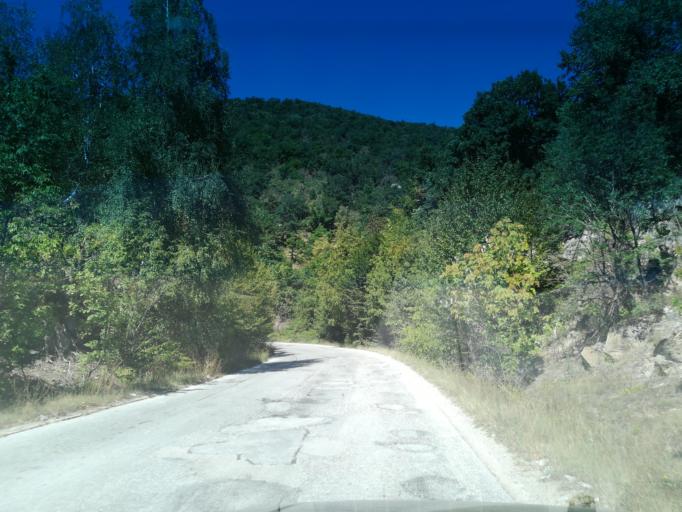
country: BG
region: Pazardzhik
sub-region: Obshtina Strelcha
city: Strelcha
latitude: 42.5486
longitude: 24.3297
